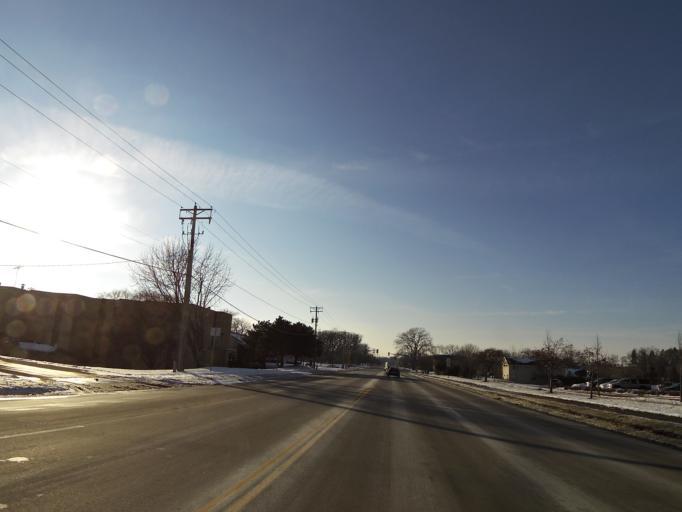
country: US
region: Minnesota
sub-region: Scott County
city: Prior Lake
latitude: 44.7174
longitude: -93.4121
